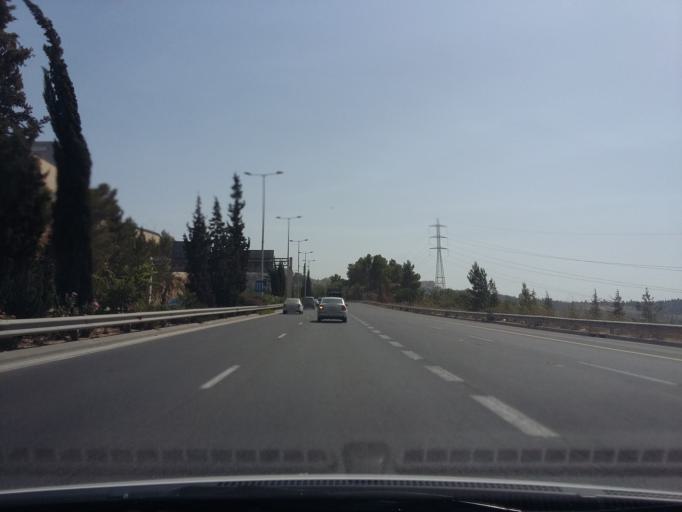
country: IL
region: Jerusalem
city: West Jerusalem
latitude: 31.8069
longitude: 35.2069
